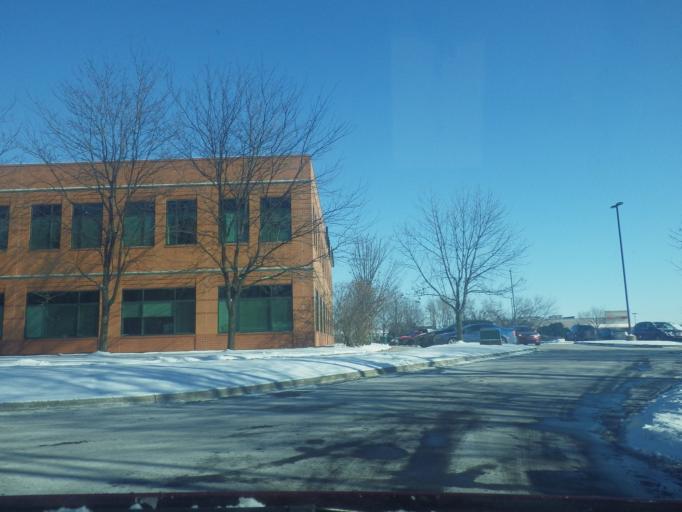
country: US
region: Indiana
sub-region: Marion County
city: Cumberland
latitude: 39.7764
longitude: -85.9955
